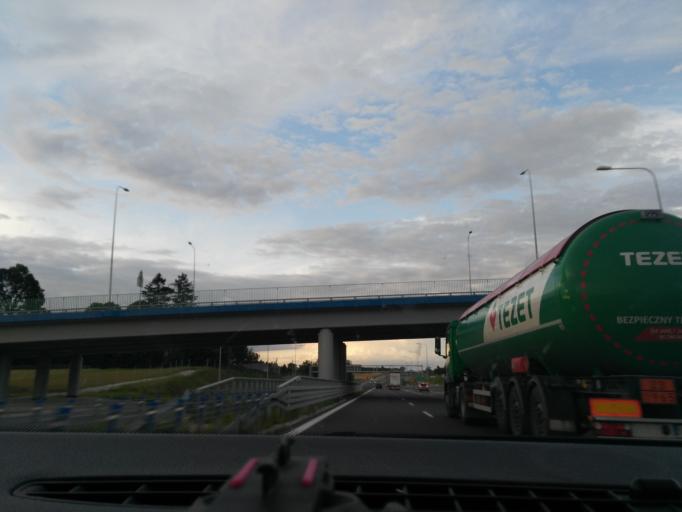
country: PL
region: Lublin Voivodeship
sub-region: Powiat lubelski
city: Jastkow
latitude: 51.2655
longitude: 22.4242
